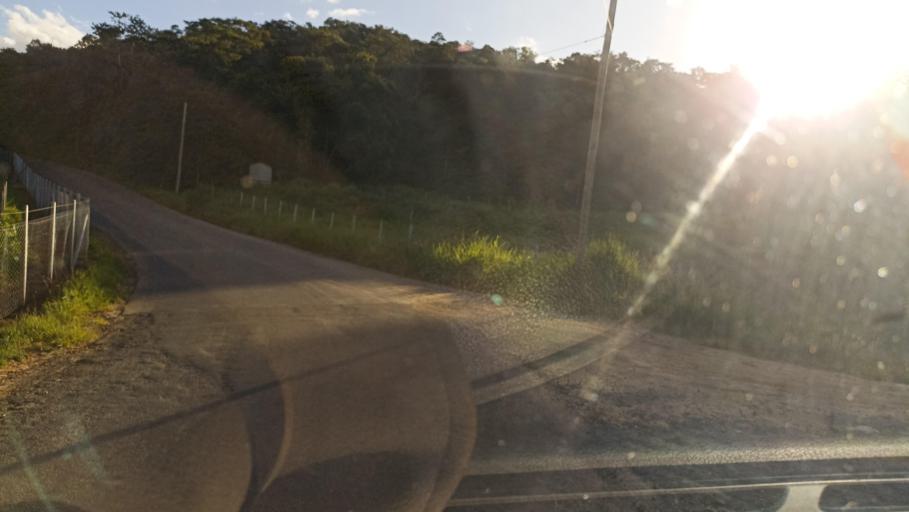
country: BR
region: Minas Gerais
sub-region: Ouro Preto
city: Ouro Preto
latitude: -20.3129
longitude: -43.6149
